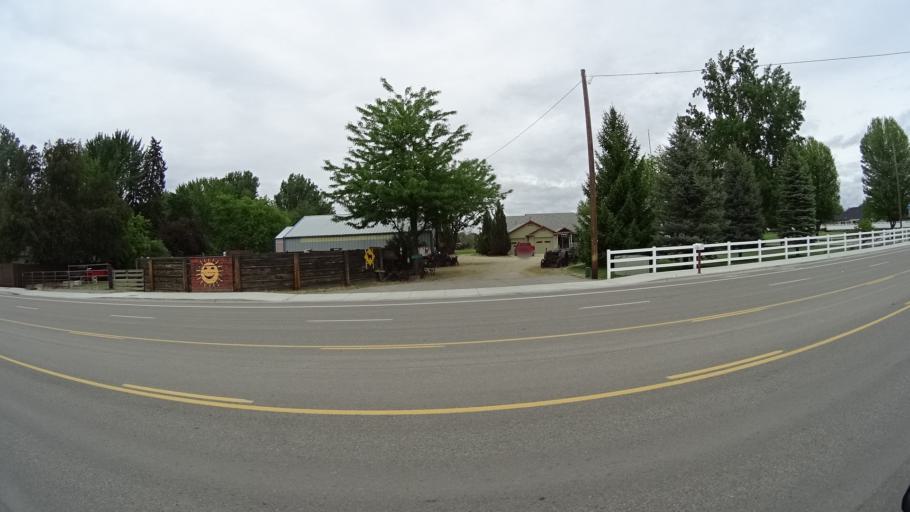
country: US
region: Idaho
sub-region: Ada County
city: Meridian
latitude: 43.6337
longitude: -116.3824
